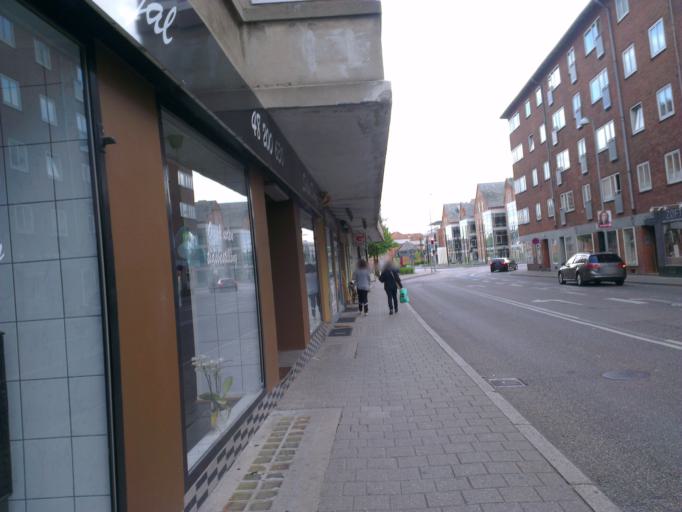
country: DK
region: Capital Region
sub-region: Hillerod Kommune
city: Hillerod
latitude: 55.9285
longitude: 12.3057
